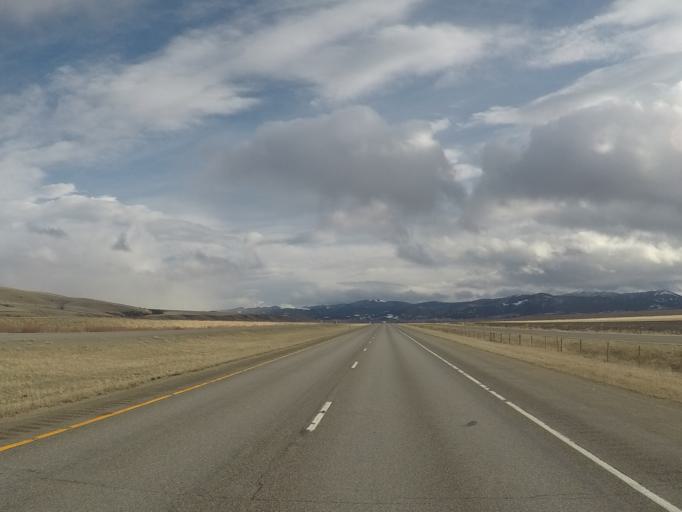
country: US
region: Montana
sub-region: Deer Lodge County
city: Warm Springs
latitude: 46.1548
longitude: -112.7927
